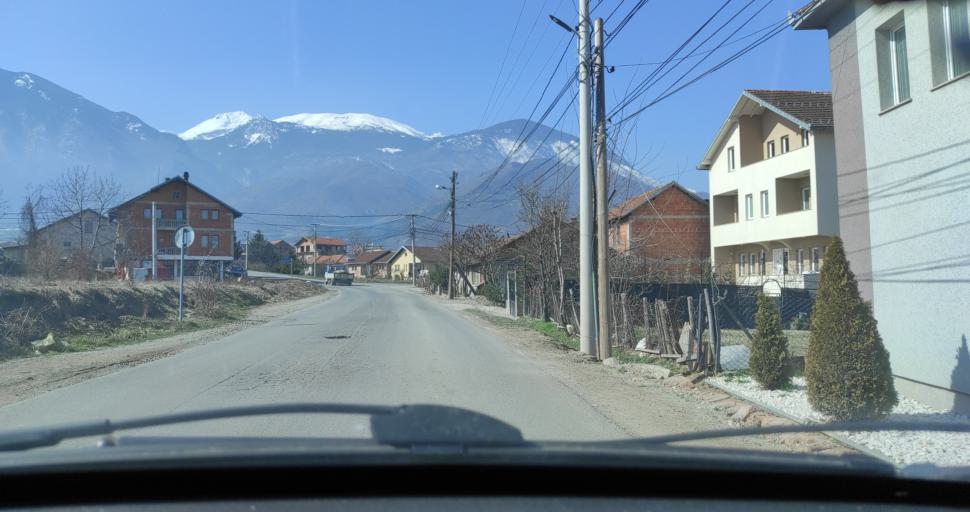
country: XK
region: Pec
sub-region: Komuna e Pejes
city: Peje
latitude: 42.6420
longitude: 20.3042
